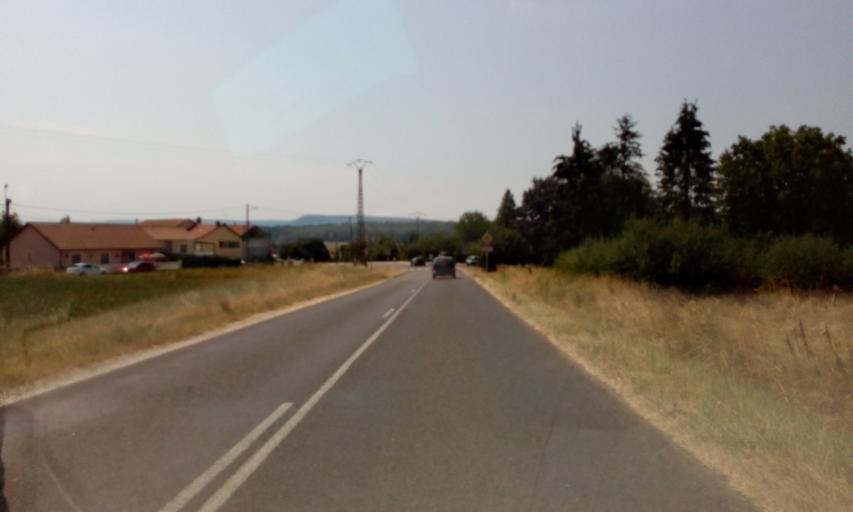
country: FR
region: Lorraine
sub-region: Departement de la Meuse
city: Montmedy
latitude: 49.4346
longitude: 5.3805
